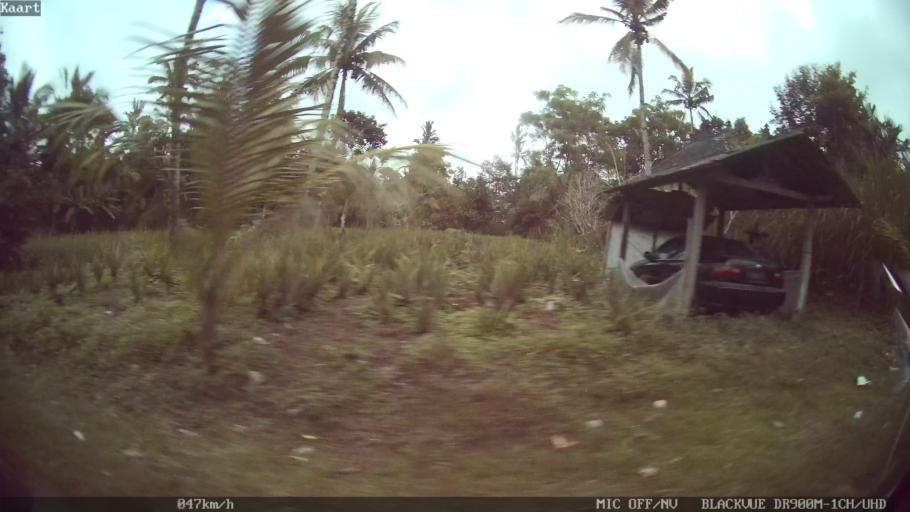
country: ID
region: Bali
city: Banjar Geriana Kangin
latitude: -8.3914
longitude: 115.4433
